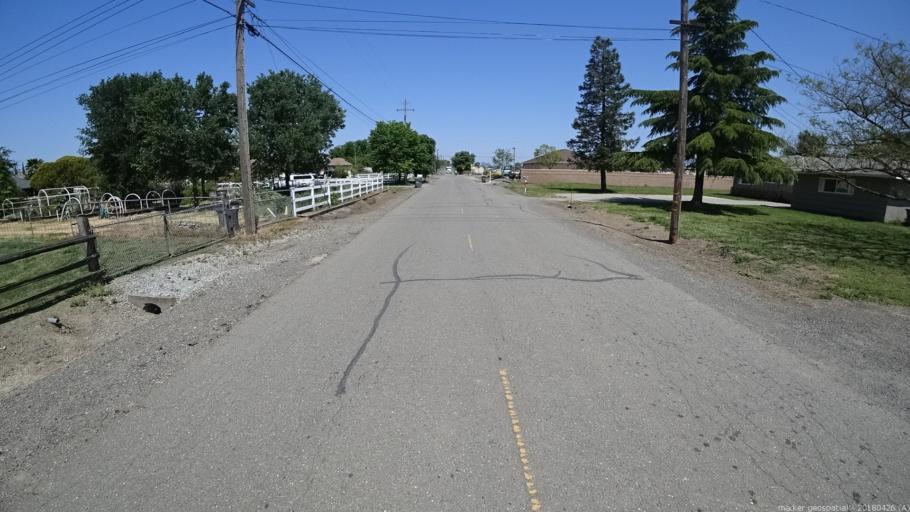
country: US
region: California
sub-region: Yolo County
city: West Sacramento
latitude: 38.5361
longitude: -121.5497
